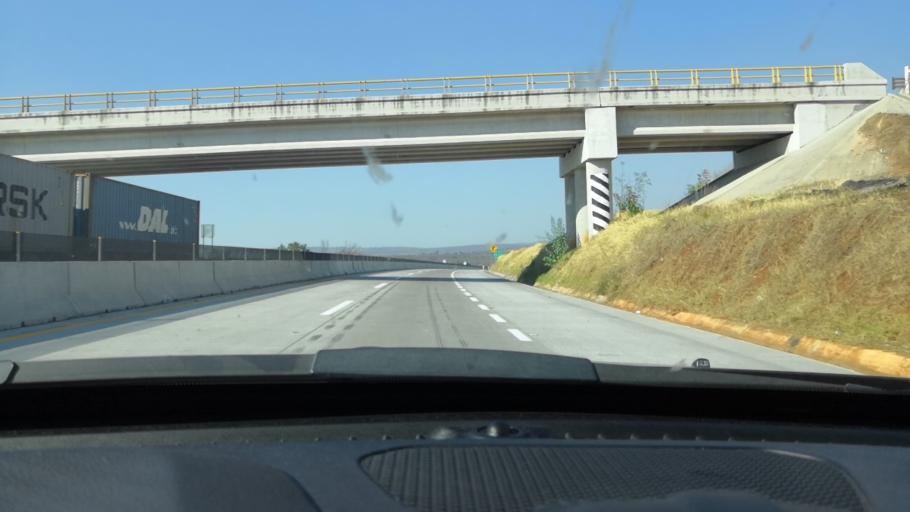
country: MX
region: Jalisco
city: Zapotlanejo
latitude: 20.6073
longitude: -103.1024
